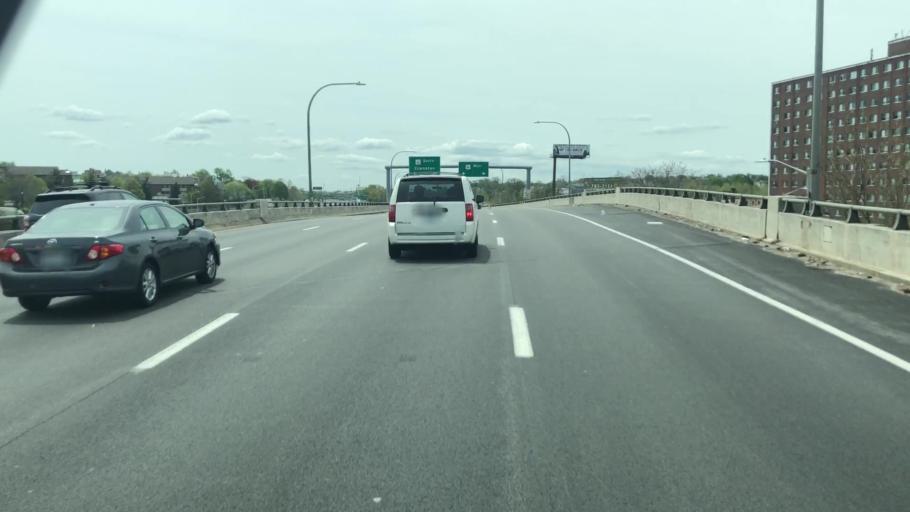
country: US
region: Rhode Island
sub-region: Providence County
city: Providence
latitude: 41.8177
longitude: -71.4389
